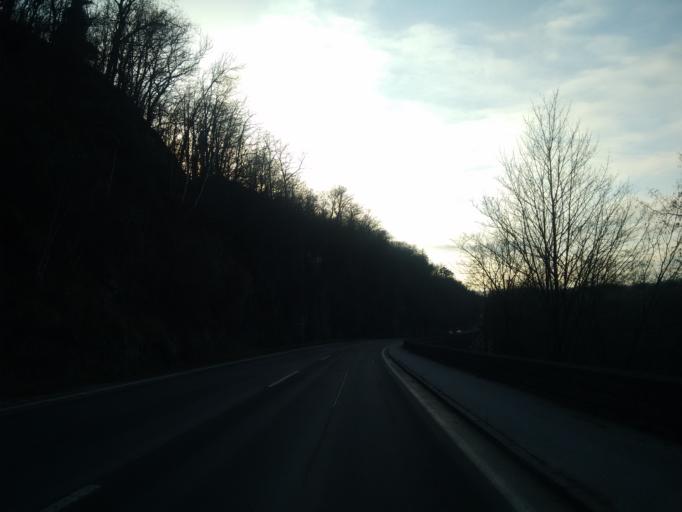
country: AT
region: Lower Austria
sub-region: Politischer Bezirk Melk
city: Emmersdorf an der Donau
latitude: 48.2327
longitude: 15.3400
